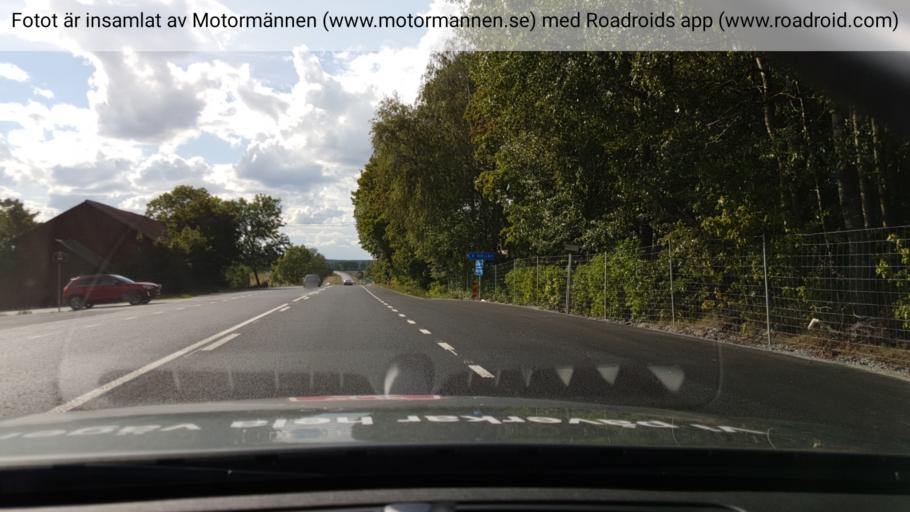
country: SE
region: Uppsala
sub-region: Enkopings Kommun
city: Grillby
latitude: 59.6611
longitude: 17.2778
